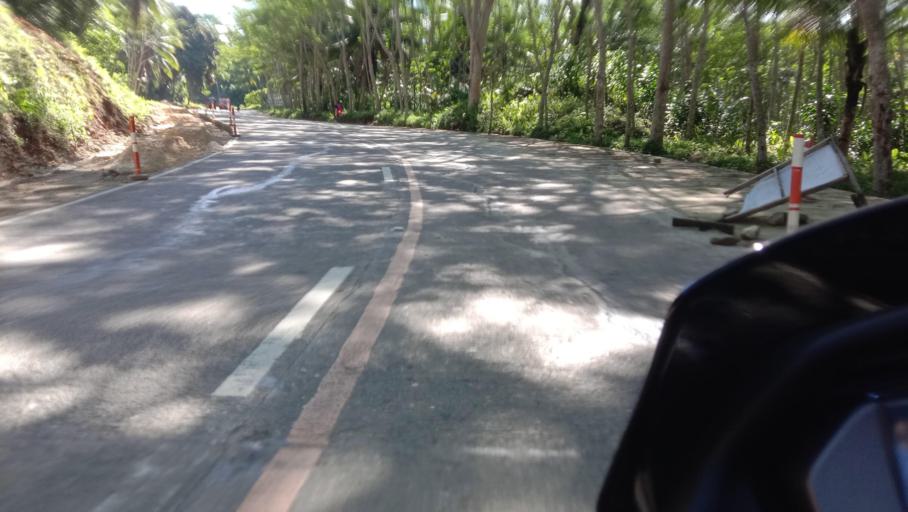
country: PH
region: Caraga
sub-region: Province of Surigao del Sur
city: Barobo
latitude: 8.5365
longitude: 126.1023
